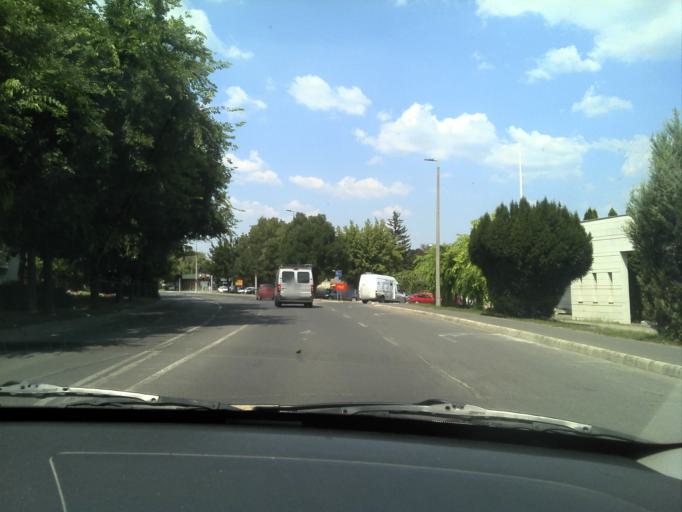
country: HU
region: Tolna
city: Tamasi
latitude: 46.6353
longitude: 18.2818
